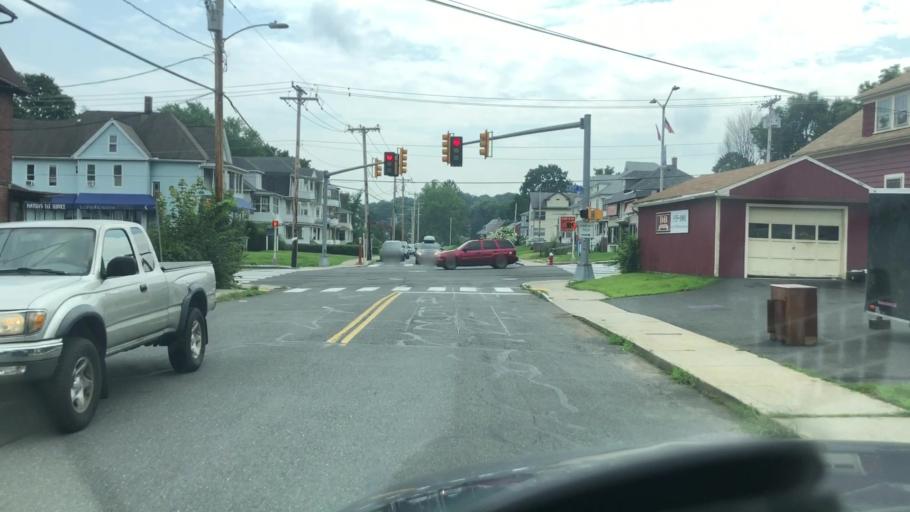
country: US
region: Massachusetts
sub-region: Hampden County
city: Holyoke
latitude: 42.1993
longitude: -72.6340
